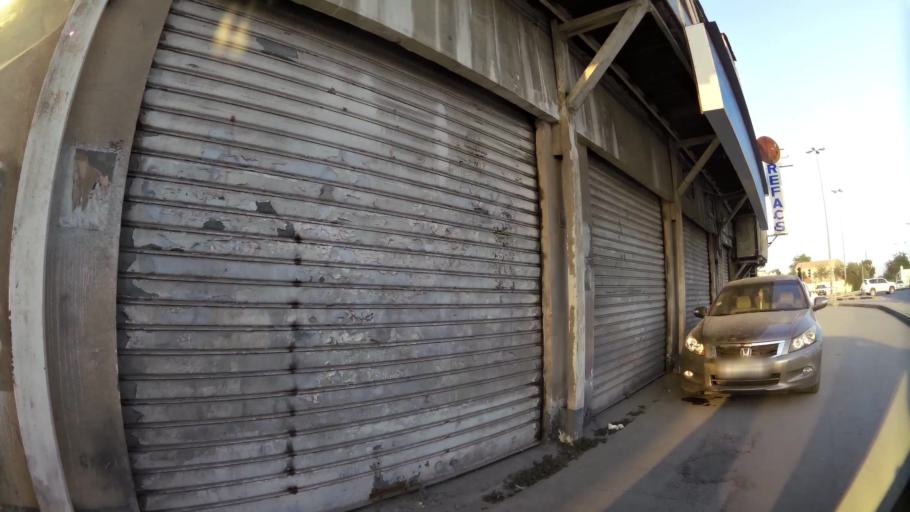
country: BH
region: Manama
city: Jidd Hafs
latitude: 26.2207
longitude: 50.5421
